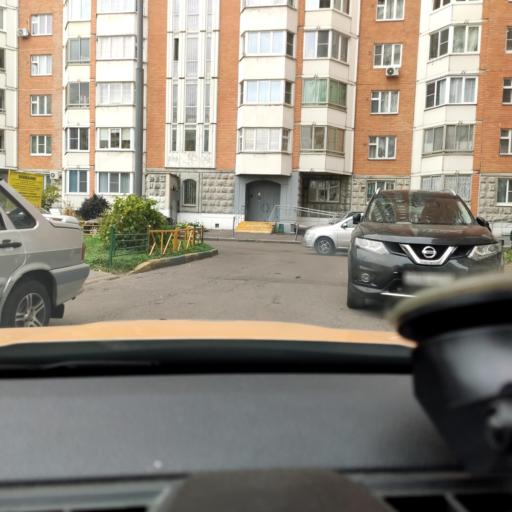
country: RU
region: Moscow
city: Kuz'minki
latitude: 55.6712
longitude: 37.7894
